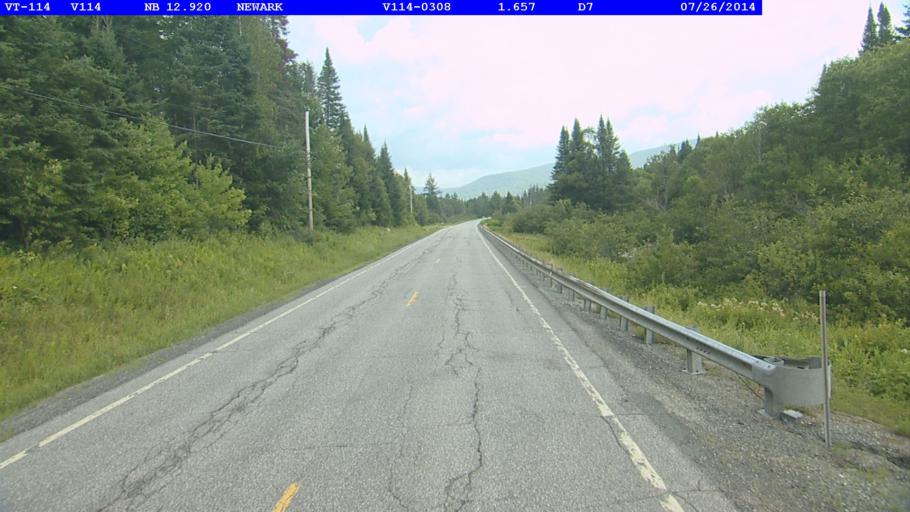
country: US
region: Vermont
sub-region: Caledonia County
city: Lyndonville
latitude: 44.6918
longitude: -71.8738
